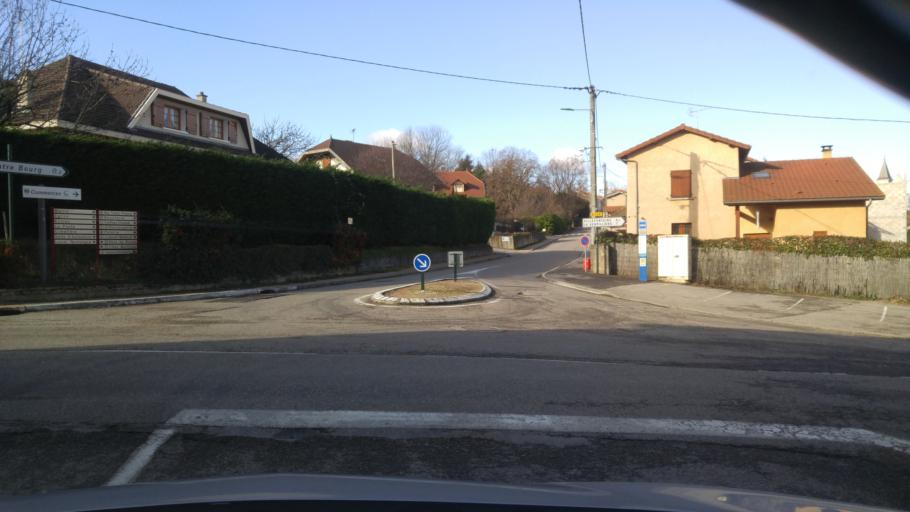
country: FR
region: Rhone-Alpes
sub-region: Departement de l'Isere
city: Roche
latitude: 45.5866
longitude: 5.1627
